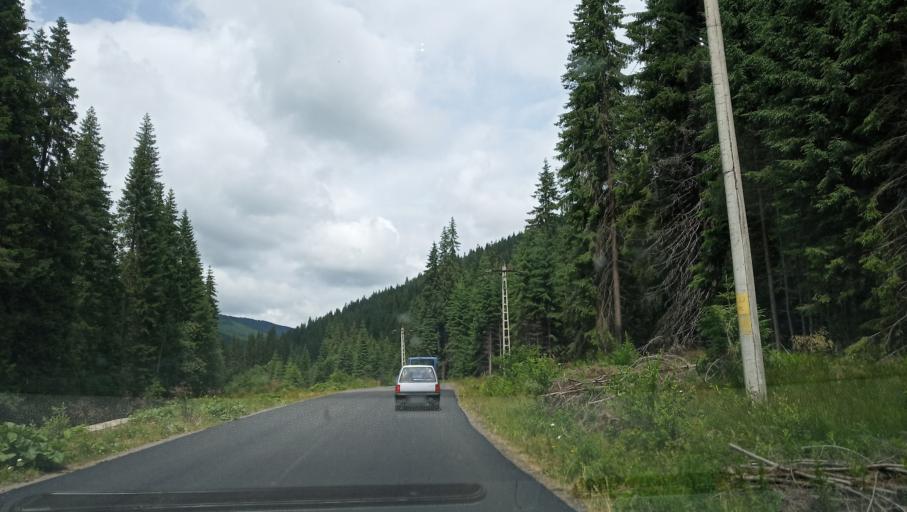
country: RO
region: Hunedoara
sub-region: Oras Petrila
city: Petrila
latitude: 45.4309
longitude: 23.6457
